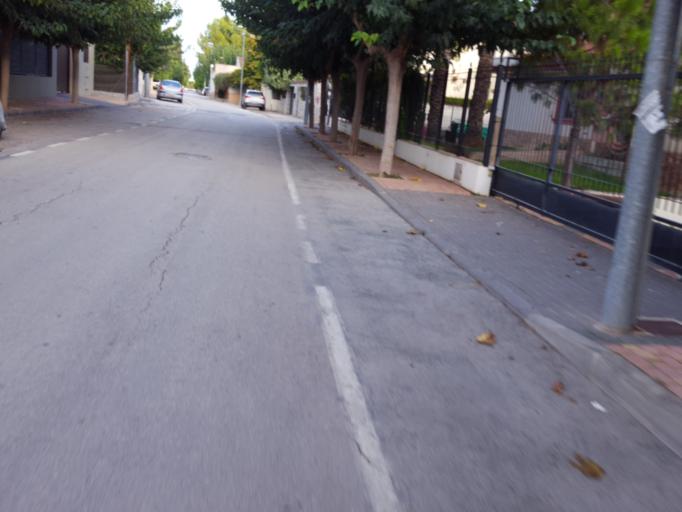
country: ES
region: Murcia
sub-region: Murcia
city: Murcia
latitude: 37.9916
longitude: -1.1721
